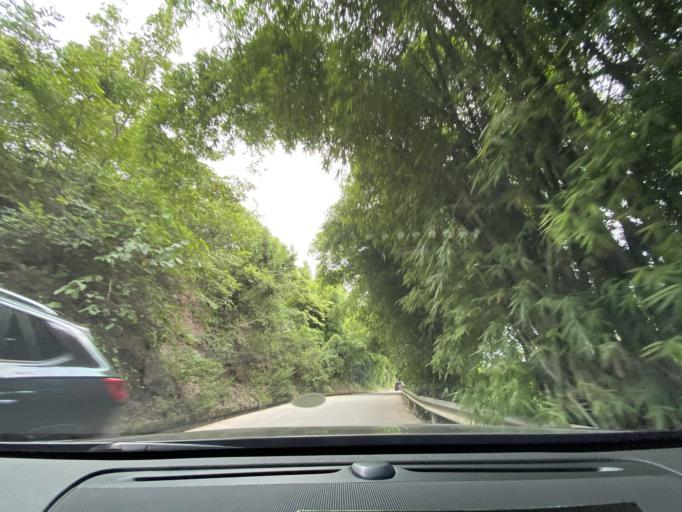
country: CN
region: Sichuan
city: Jiancheng
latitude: 30.4414
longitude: 104.5442
